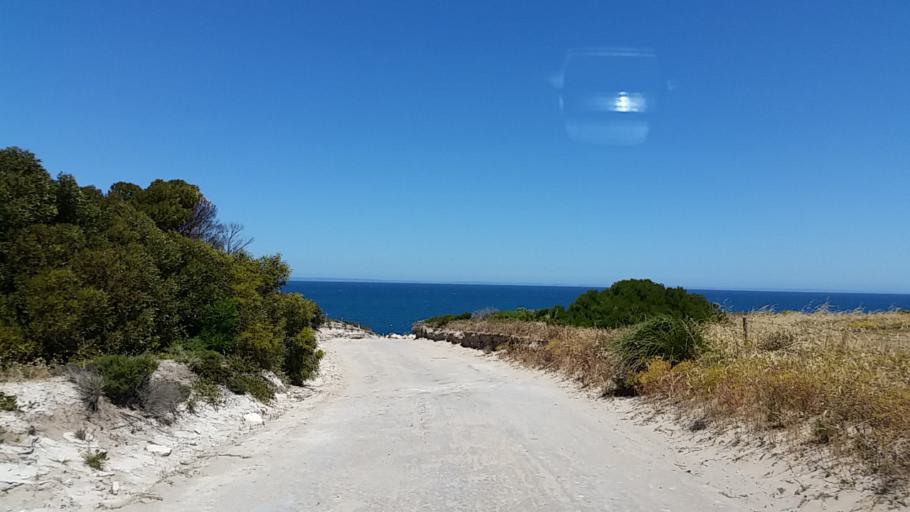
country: AU
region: South Australia
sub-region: Yorke Peninsula
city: Honiton
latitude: -35.2359
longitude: 137.1634
